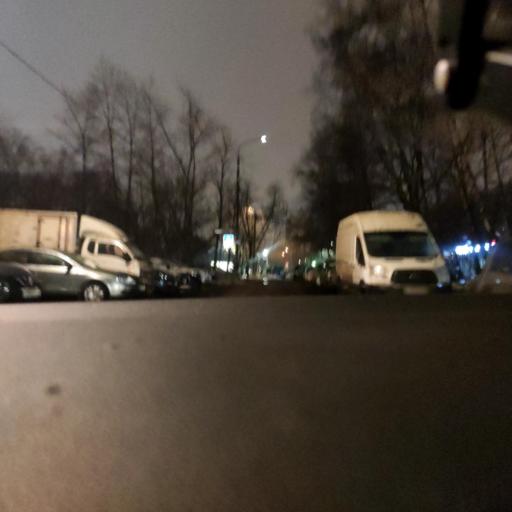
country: RU
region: Moscow
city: Slobodka
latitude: 55.8674
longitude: 37.5709
